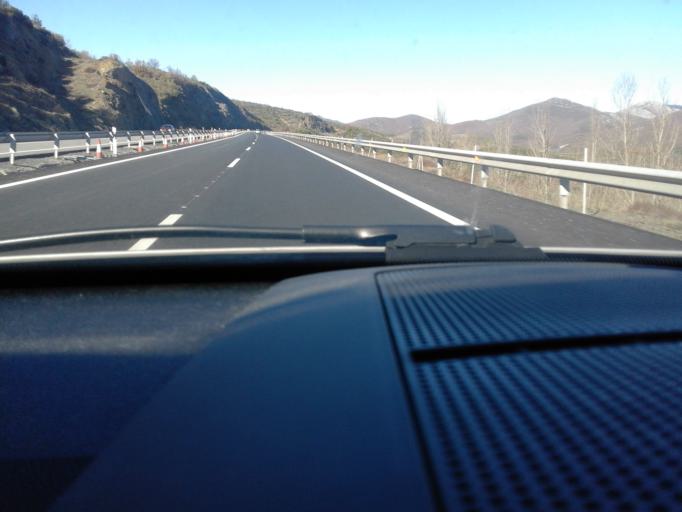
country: ES
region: Castille and Leon
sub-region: Provincia de Leon
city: Soto y Amio
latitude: 42.7970
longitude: -5.8253
